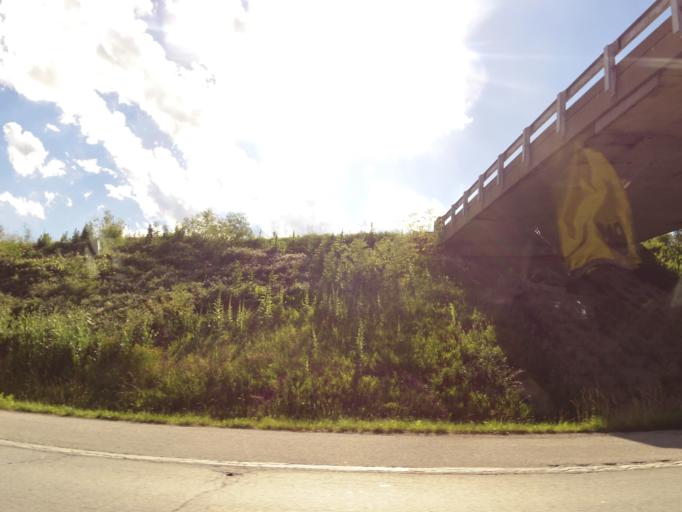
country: US
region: Missouri
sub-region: Marion County
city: Palmyra
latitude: 39.8094
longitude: -91.5161
